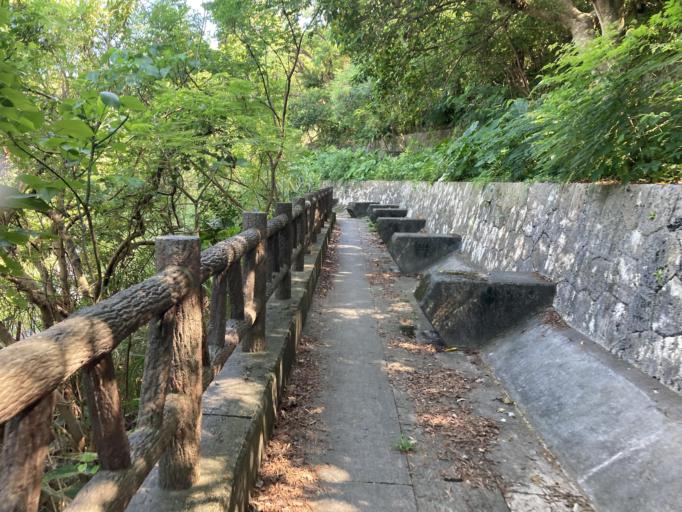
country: JP
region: Okinawa
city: Naha-shi
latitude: 26.2112
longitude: 127.7178
